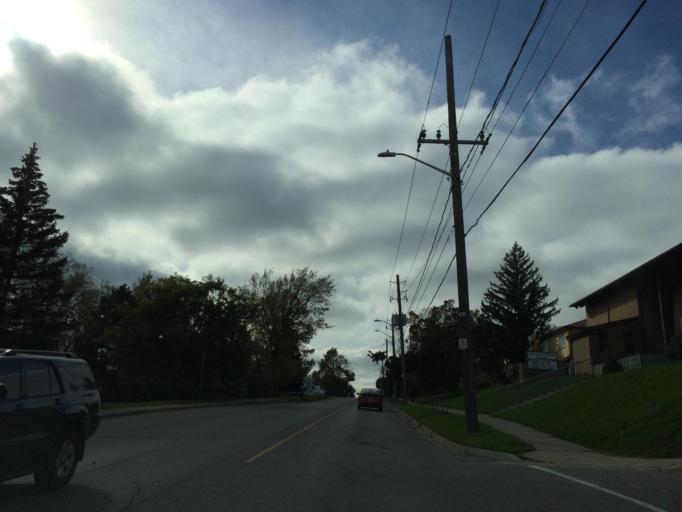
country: CA
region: Ontario
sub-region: Wellington County
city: Guelph
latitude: 43.5380
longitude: -80.2669
